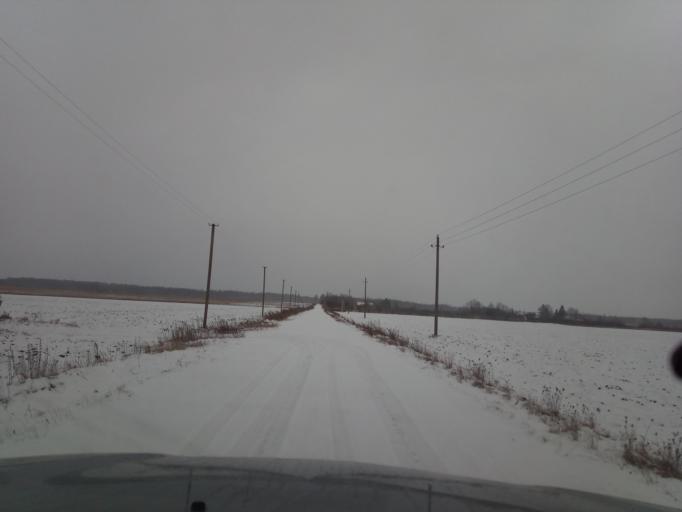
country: LT
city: Ramygala
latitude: 55.5888
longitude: 24.3578
